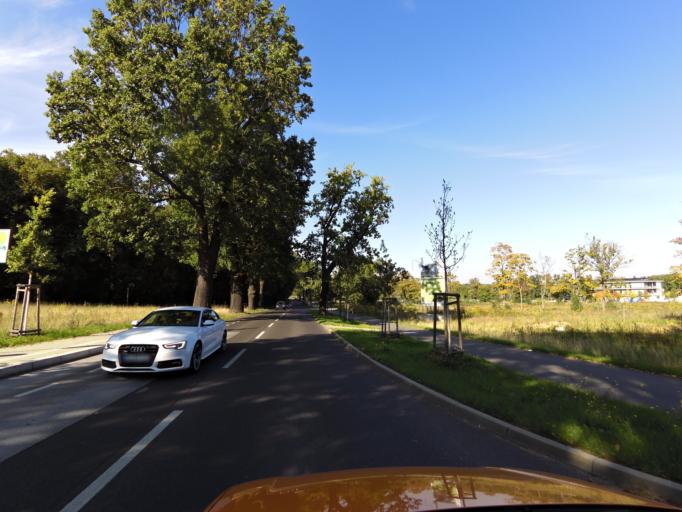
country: DE
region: Brandenburg
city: Potsdam
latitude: 52.4328
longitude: 13.0533
